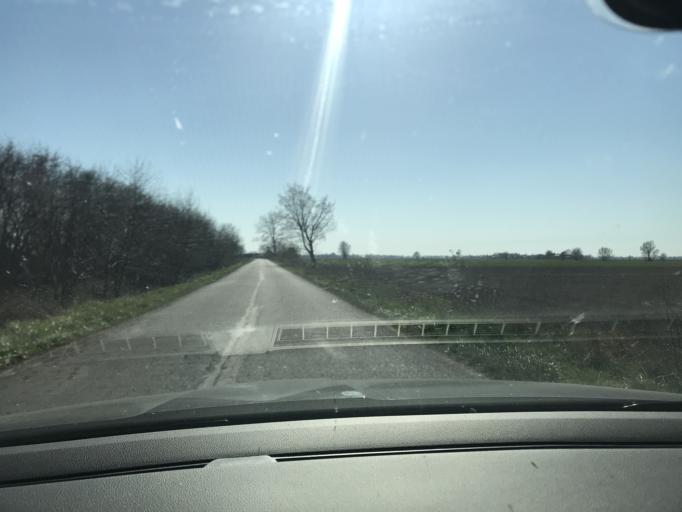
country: PL
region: Pomeranian Voivodeship
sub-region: Powiat nowodworski
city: Sztutowo
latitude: 54.3094
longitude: 19.1557
